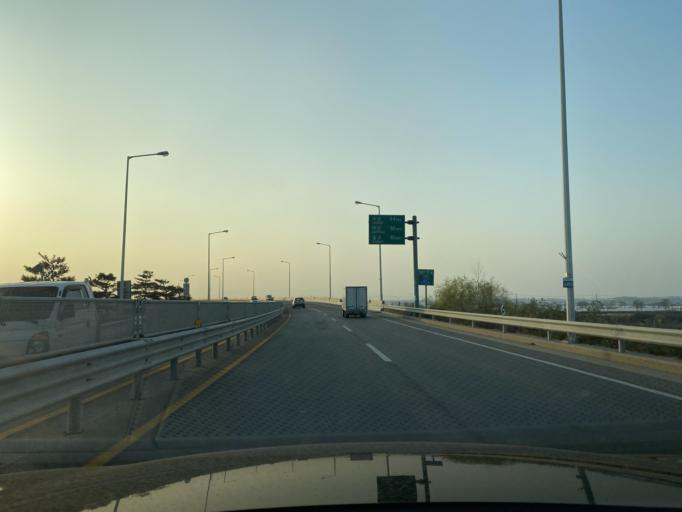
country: KR
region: Chungcheongnam-do
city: Yesan
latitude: 36.7044
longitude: 126.8271
